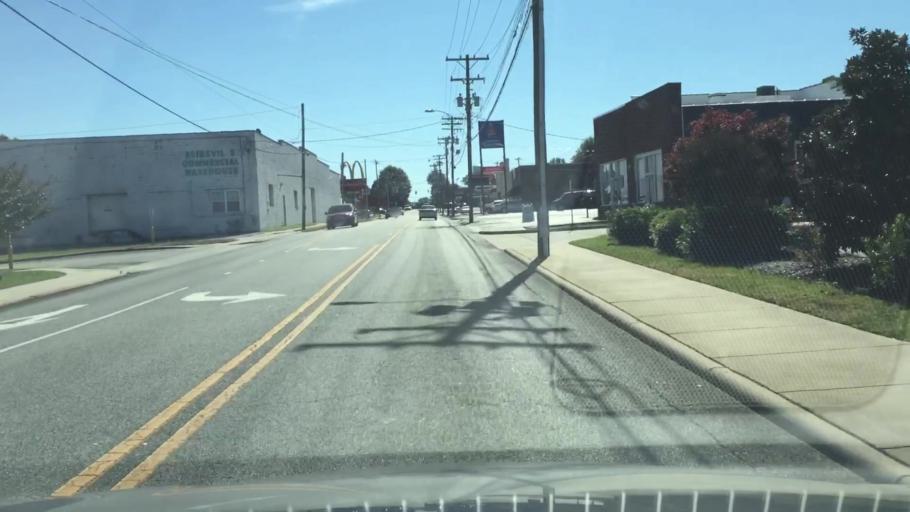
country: US
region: North Carolina
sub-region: Rockingham County
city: Reidsville
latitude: 36.3546
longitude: -79.6647
